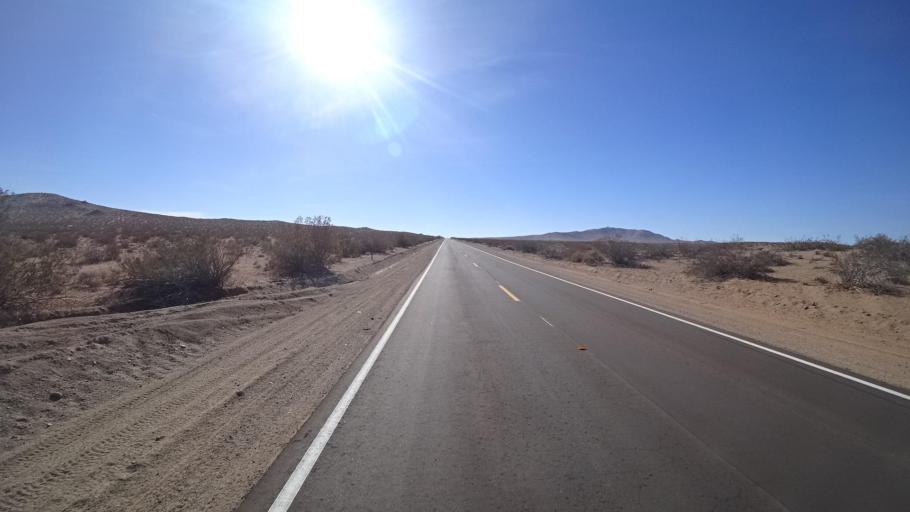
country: US
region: California
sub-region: Kern County
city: Ridgecrest
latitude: 35.5062
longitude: -117.6171
